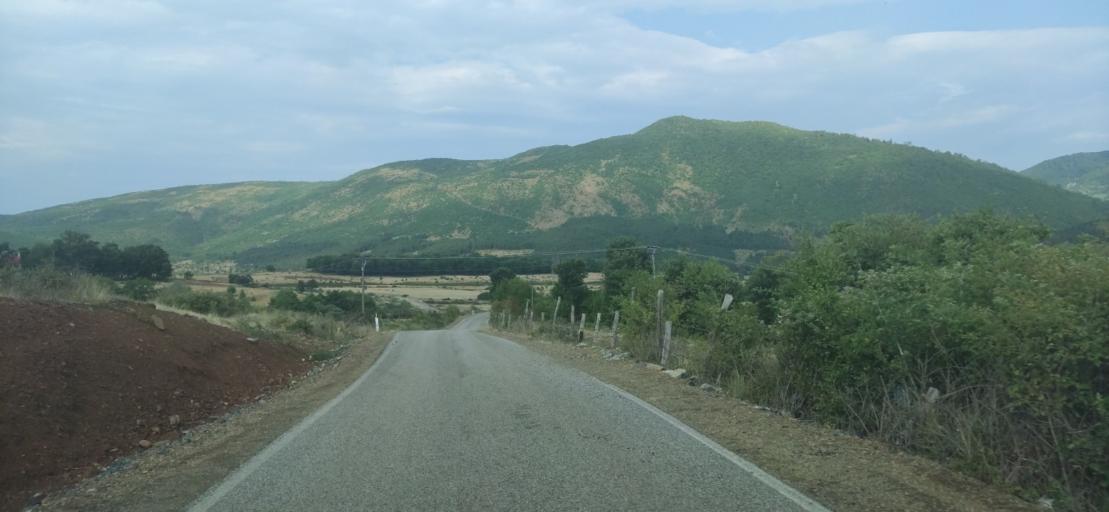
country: AL
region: Shkoder
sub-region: Rrethi i Pukes
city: Iballe
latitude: 42.1875
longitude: 19.9995
